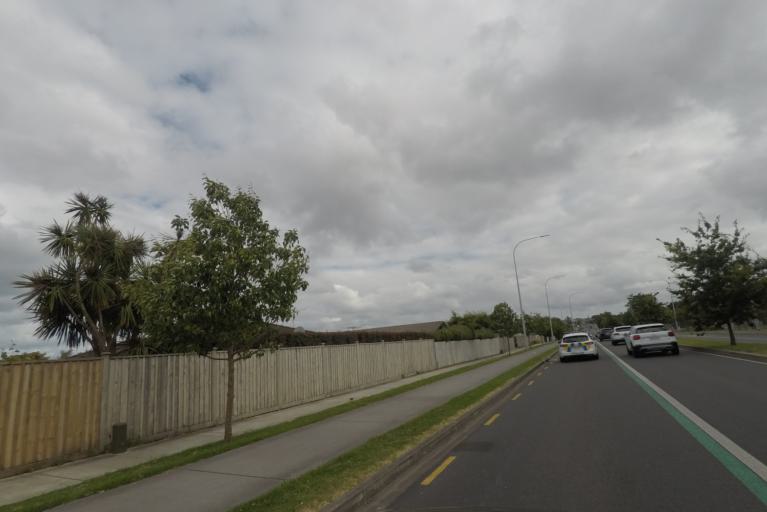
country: NZ
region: Auckland
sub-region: Auckland
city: Rothesay Bay
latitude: -36.7400
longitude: 174.6926
